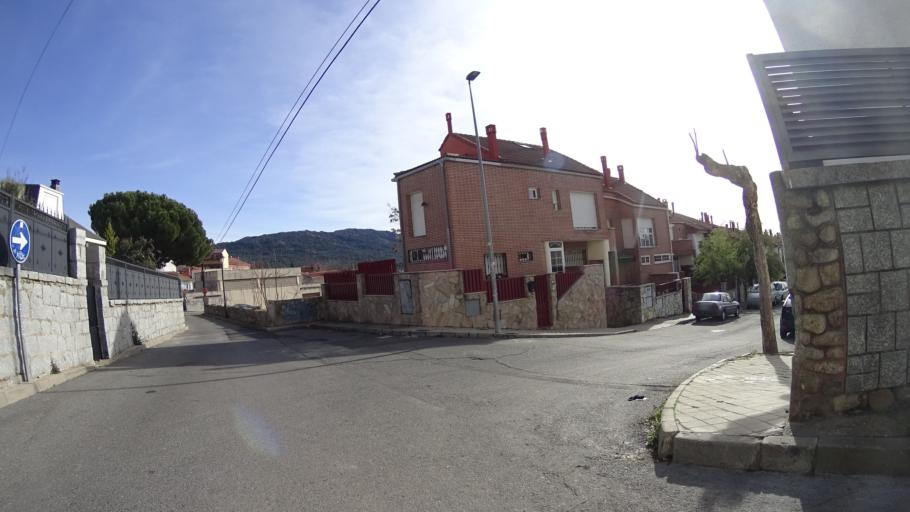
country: ES
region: Madrid
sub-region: Provincia de Madrid
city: Moralzarzal
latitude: 40.6790
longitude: -3.9741
